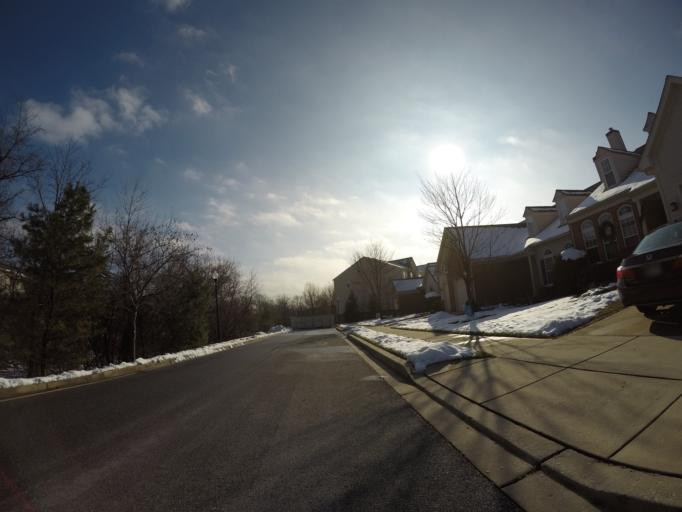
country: US
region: Maryland
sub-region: Howard County
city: Ilchester
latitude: 39.2118
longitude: -76.7817
